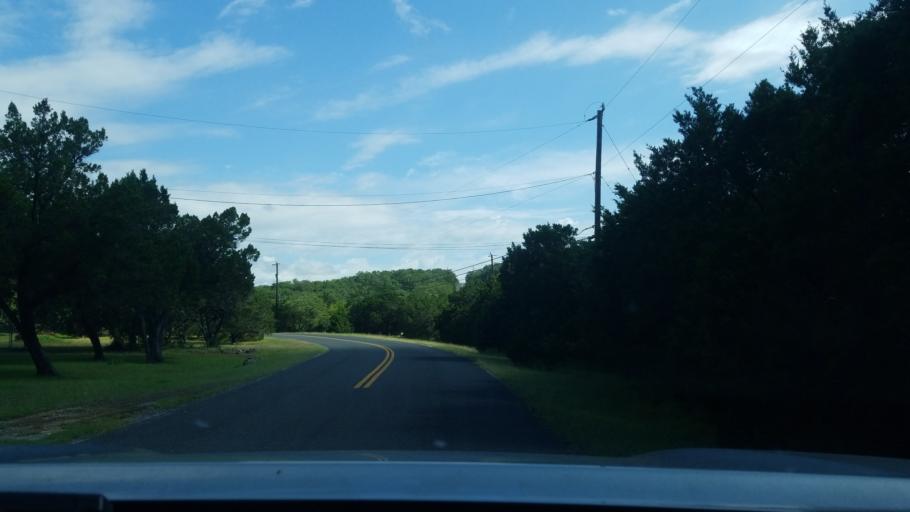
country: US
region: Texas
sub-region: Comal County
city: Bulverde
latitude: 29.7533
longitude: -98.4427
